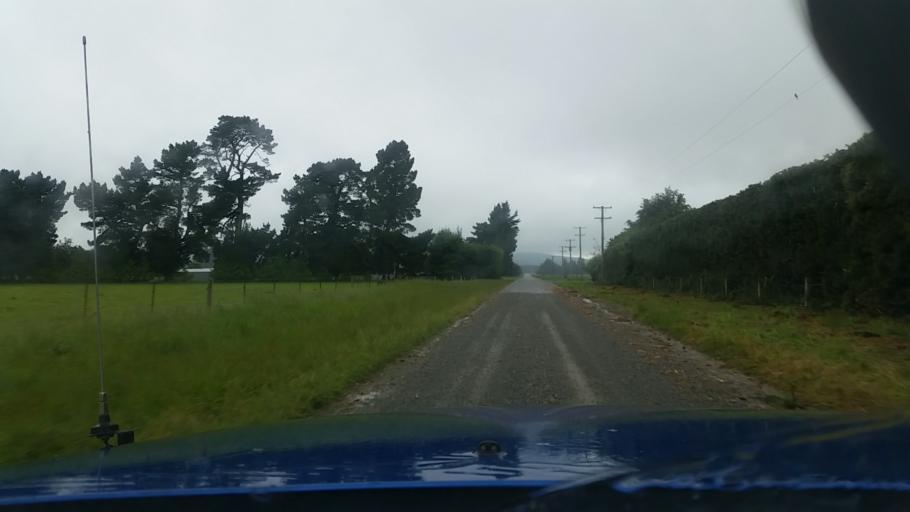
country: NZ
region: Canterbury
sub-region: Ashburton District
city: Methven
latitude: -43.7602
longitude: 171.2705
